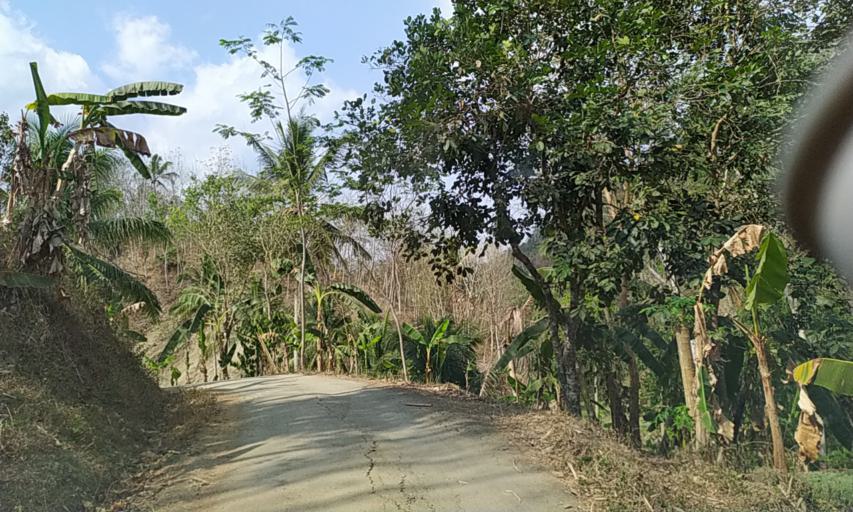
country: ID
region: Central Java
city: Bantarmangu
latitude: -7.3321
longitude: 108.9003
